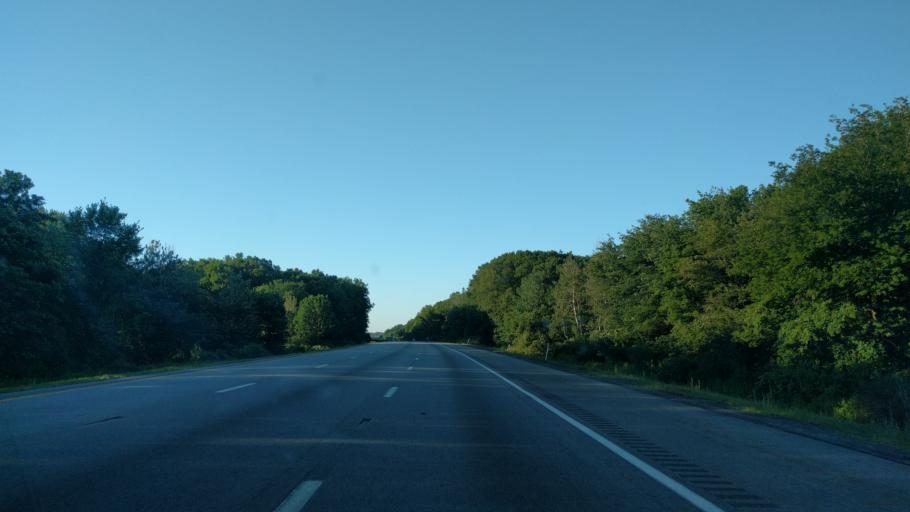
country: US
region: Massachusetts
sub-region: Middlesex County
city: Marlborough
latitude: 42.3300
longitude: -71.5753
